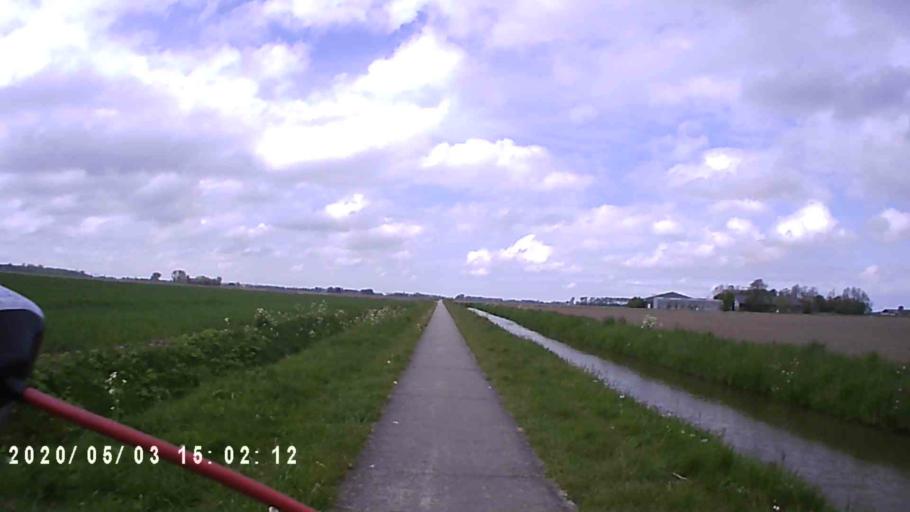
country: NL
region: Groningen
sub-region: Gemeente Zuidhorn
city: Oldehove
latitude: 53.3625
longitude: 6.4449
